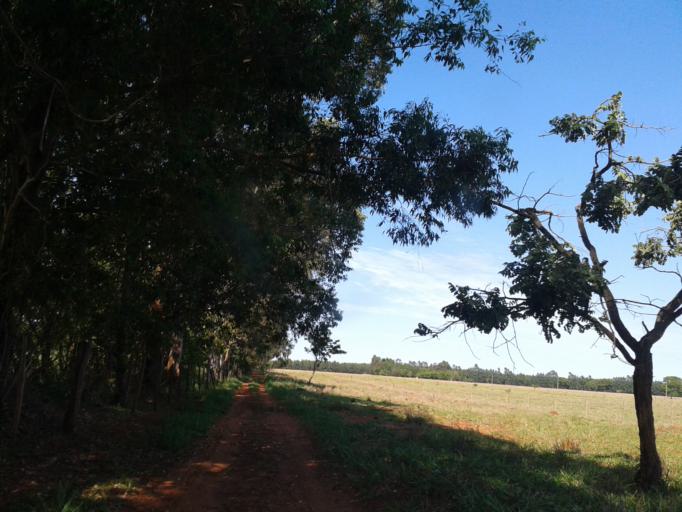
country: BR
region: Minas Gerais
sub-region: Centralina
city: Centralina
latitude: -18.7200
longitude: -49.1584
